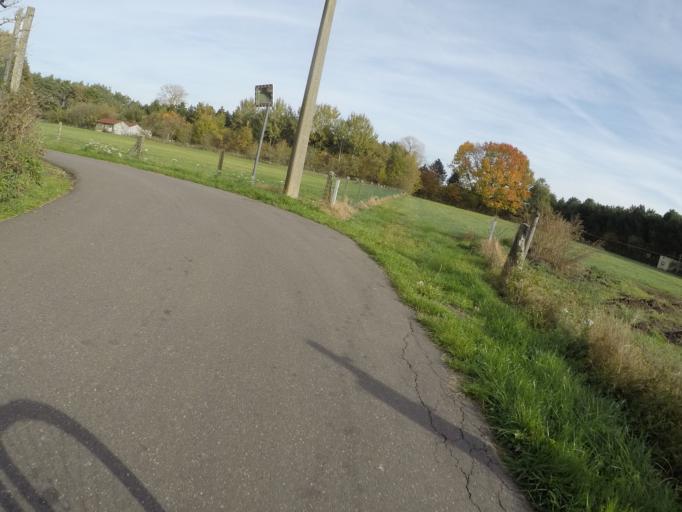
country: BE
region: Flanders
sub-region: Provincie Vlaams-Brabant
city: Begijnendijk
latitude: 51.0354
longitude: 4.7847
